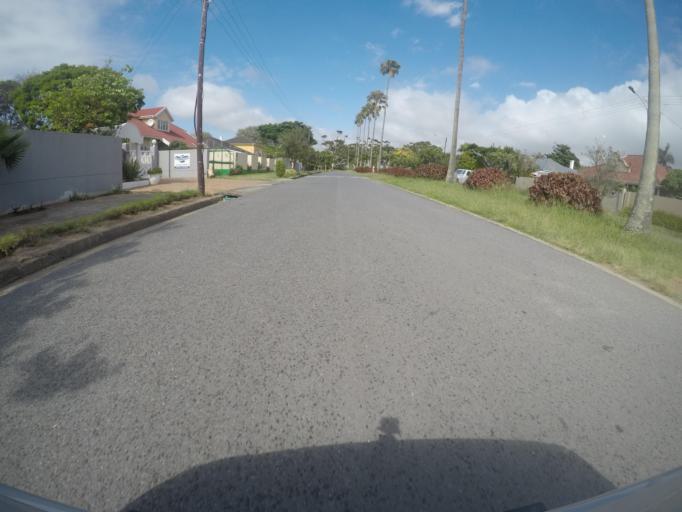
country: ZA
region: Eastern Cape
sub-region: Buffalo City Metropolitan Municipality
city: East London
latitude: -32.9928
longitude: 27.8977
